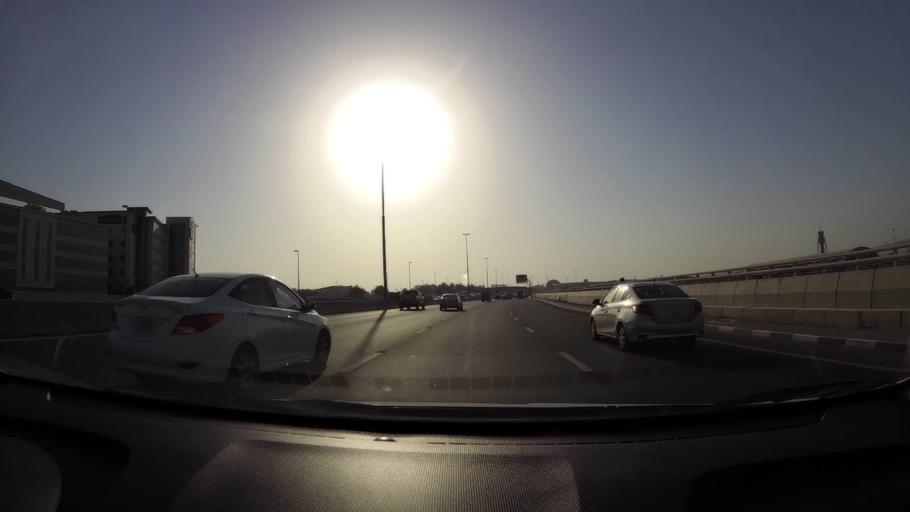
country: AE
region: Ash Shariqah
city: Sharjah
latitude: 25.2434
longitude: 55.3601
